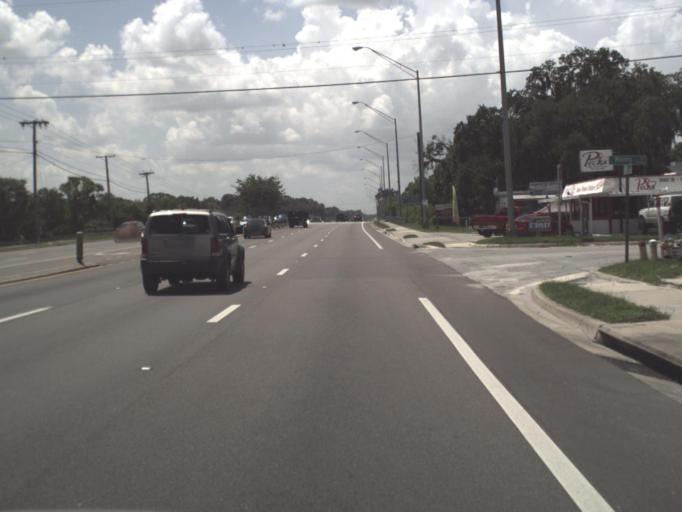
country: US
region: Florida
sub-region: Hillsborough County
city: Riverview
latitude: 27.8711
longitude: -82.3268
